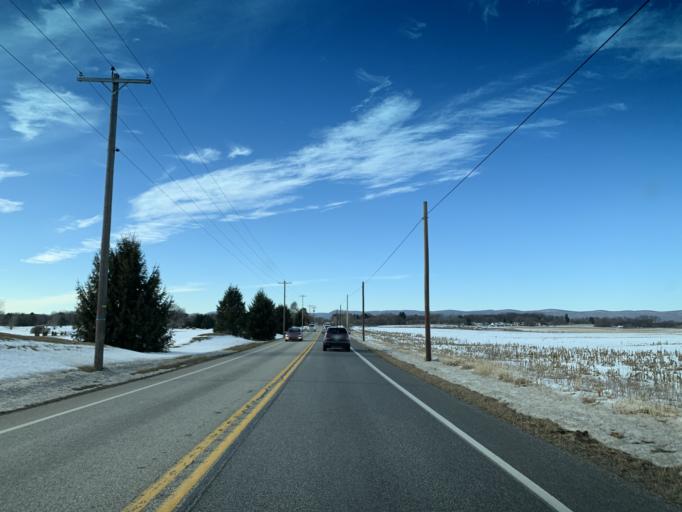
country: US
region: Pennsylvania
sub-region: Cumberland County
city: Boiling Springs
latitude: 40.1845
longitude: -77.1455
